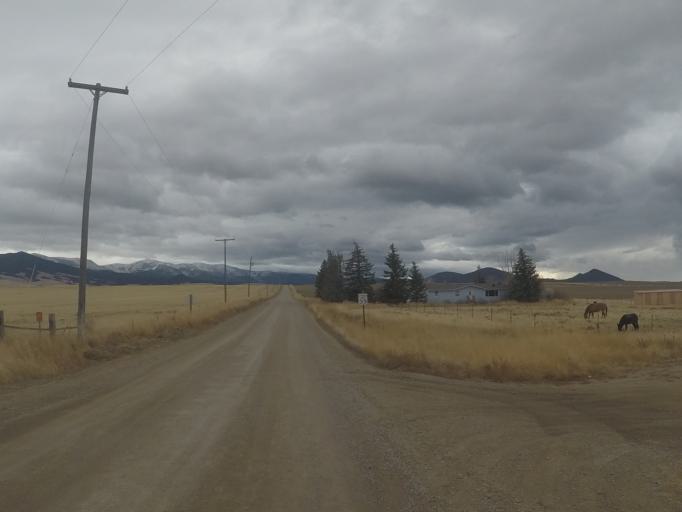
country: US
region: Montana
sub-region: Lewis and Clark County
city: East Helena
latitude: 46.5857
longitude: -111.8726
